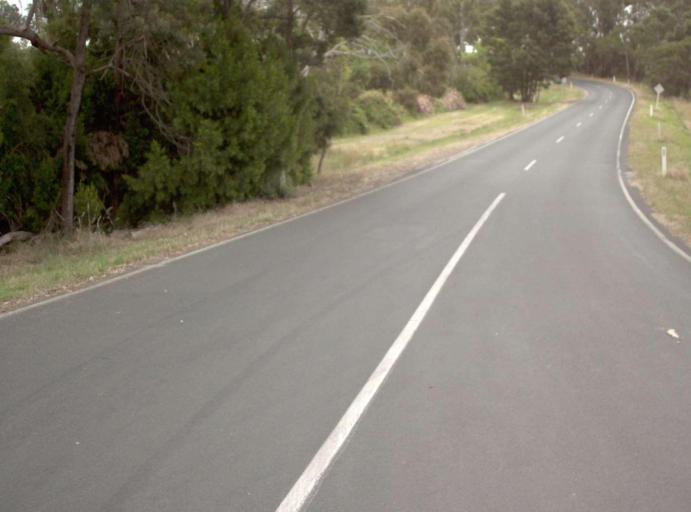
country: AU
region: Victoria
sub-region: Wellington
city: Sale
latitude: -38.5263
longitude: 146.8704
